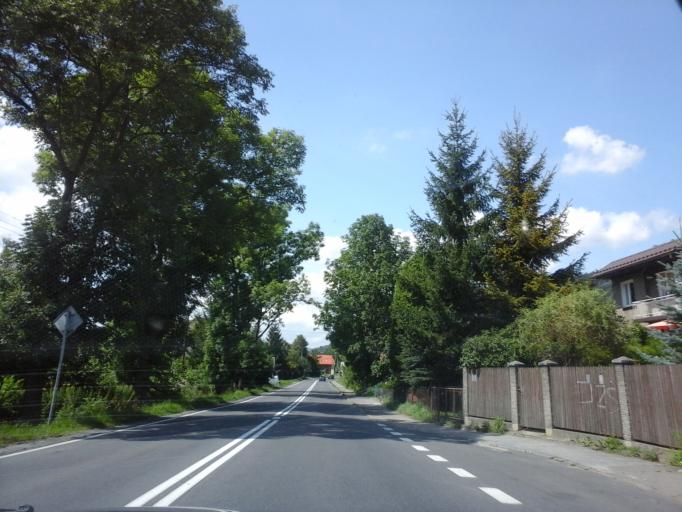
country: PL
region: Lesser Poland Voivodeship
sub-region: Powiat suski
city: Makow Podhalanski
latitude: 49.7312
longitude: 19.6651
